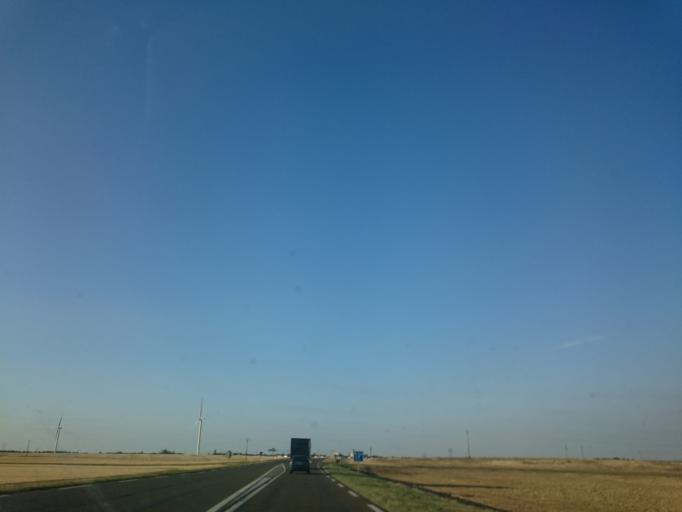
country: FR
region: Centre
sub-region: Departement d'Eure-et-Loir
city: Toury
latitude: 48.1649
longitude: 1.9150
